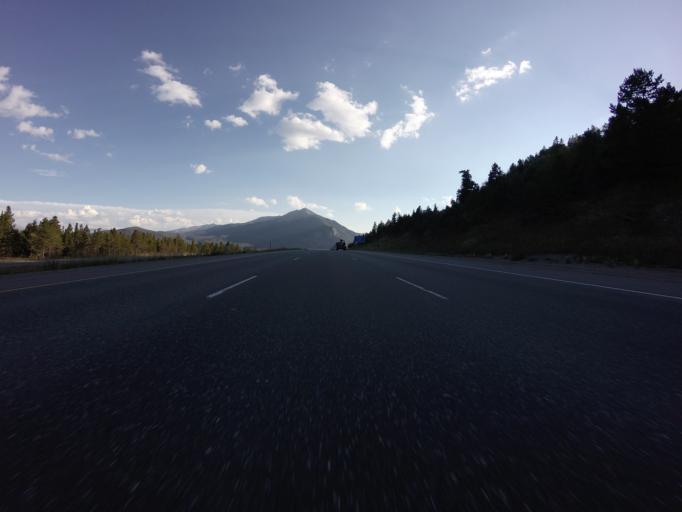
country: US
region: Colorado
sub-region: Summit County
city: Silverthorne
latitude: 39.6076
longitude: -106.0814
